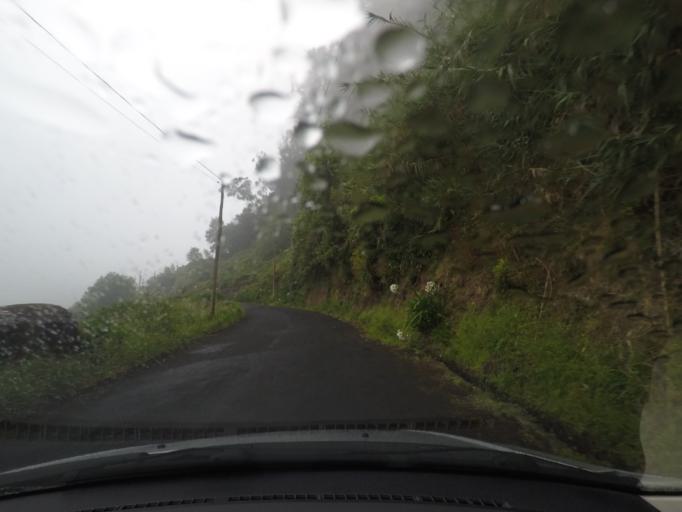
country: PT
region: Madeira
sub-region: Santana
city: Santana
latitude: 32.7534
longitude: -16.8765
